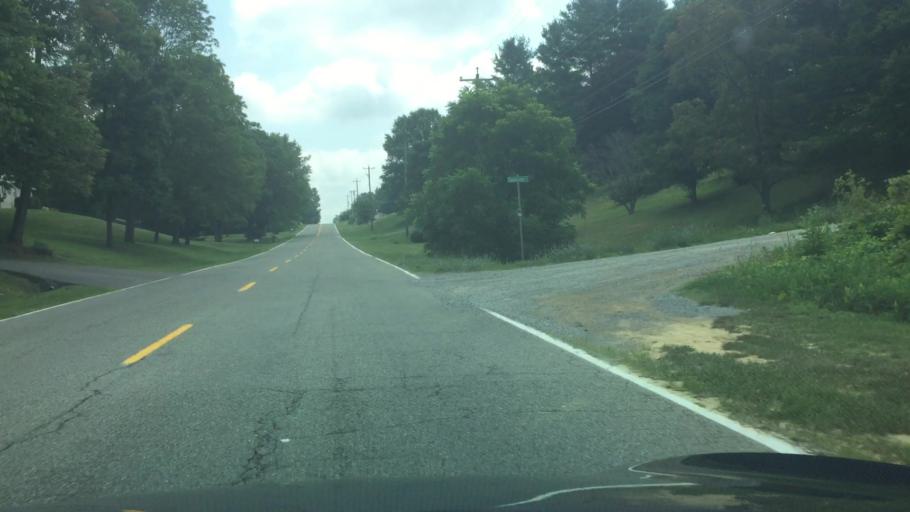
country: US
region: Virginia
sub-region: Pulaski County
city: Pulaski
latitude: 36.9562
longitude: -80.8704
